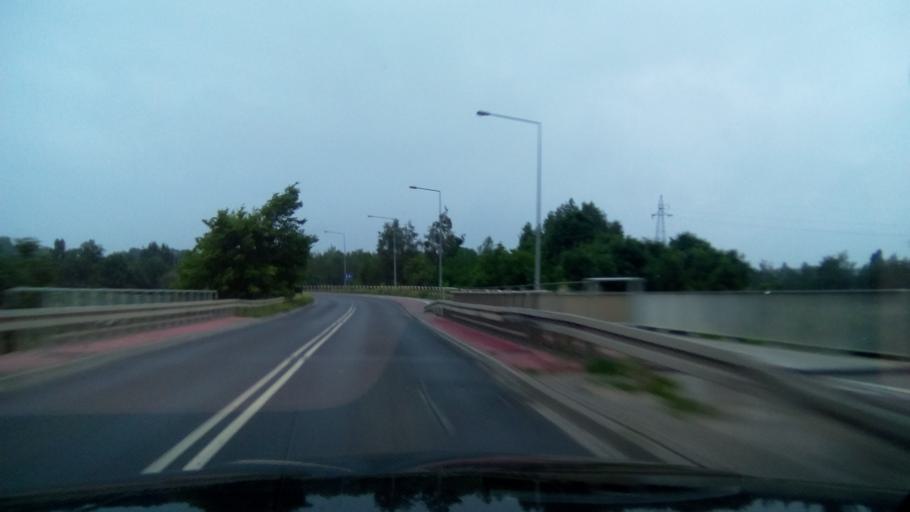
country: PL
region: Greater Poland Voivodeship
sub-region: Powiat poznanski
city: Swarzedz
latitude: 52.4253
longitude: 17.0806
